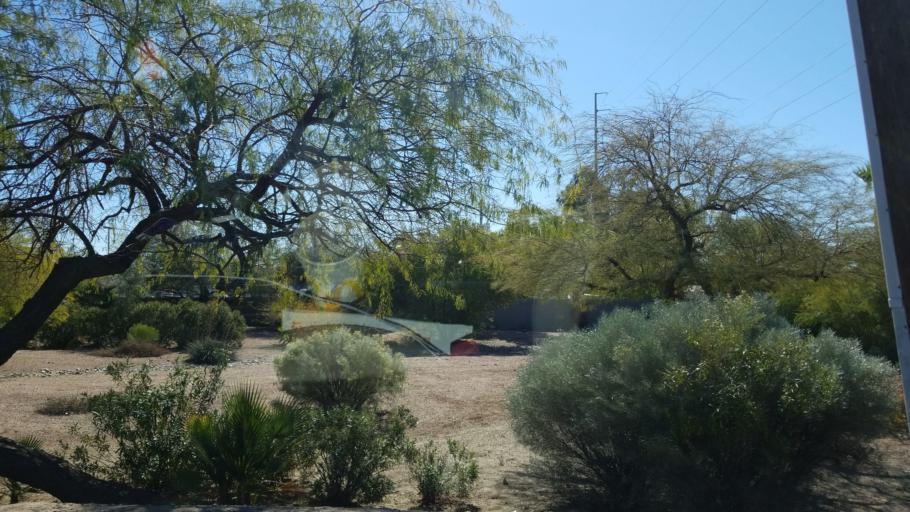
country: US
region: Arizona
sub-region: Maricopa County
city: Chandler
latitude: 33.3206
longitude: -111.8369
